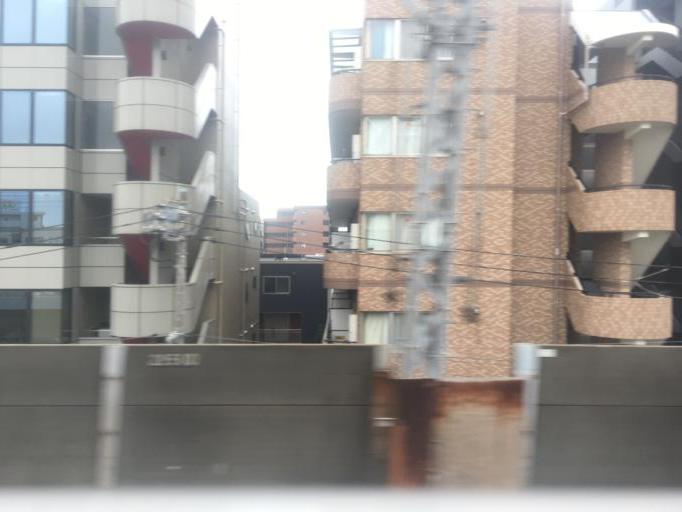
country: JP
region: Tokyo
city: Urayasu
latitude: 35.6634
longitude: 139.8757
